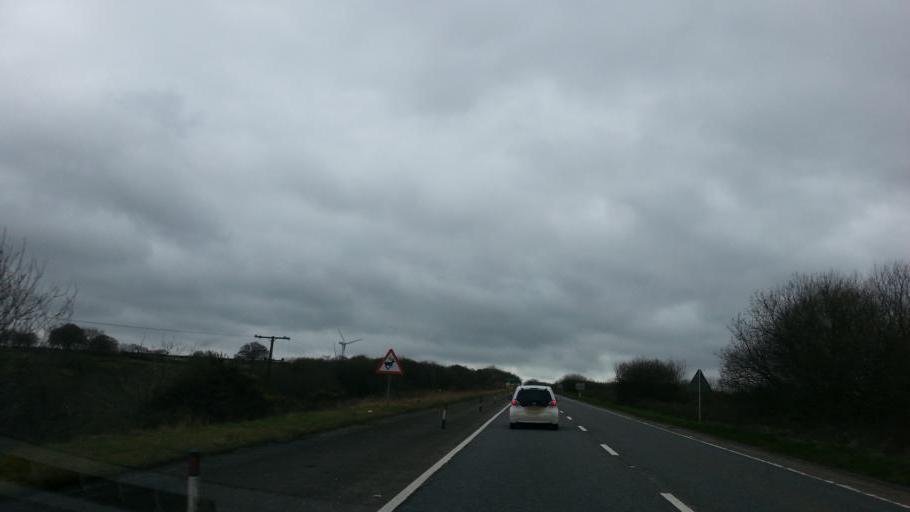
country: GB
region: England
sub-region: Devon
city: South Molton
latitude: 50.9819
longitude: -3.6613
